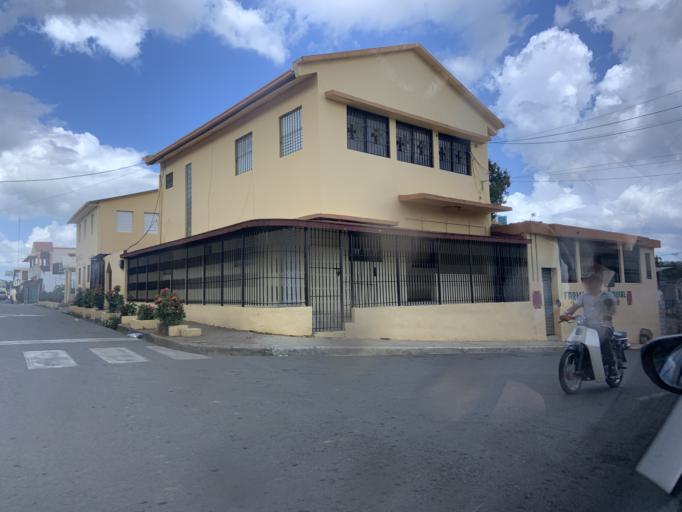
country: DO
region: Monte Plata
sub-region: Yamasa
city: Yamasa
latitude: 18.7701
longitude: -70.0252
